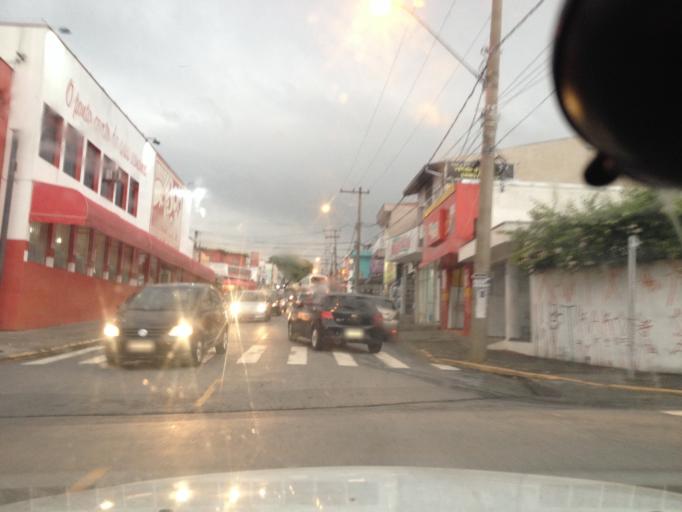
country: BR
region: Sao Paulo
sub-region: Salto
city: Salto
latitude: -23.1931
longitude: -47.2736
